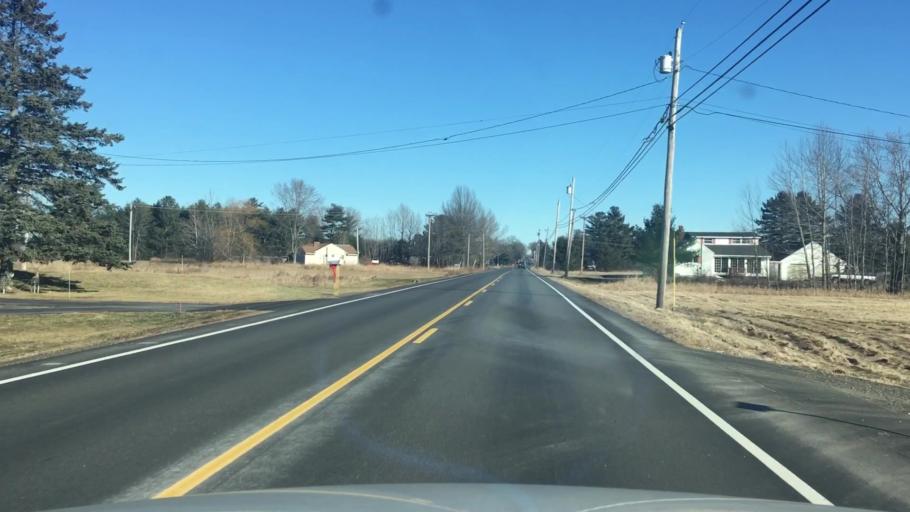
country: US
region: Maine
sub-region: Kennebec County
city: Benton
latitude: 44.6052
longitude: -69.5344
